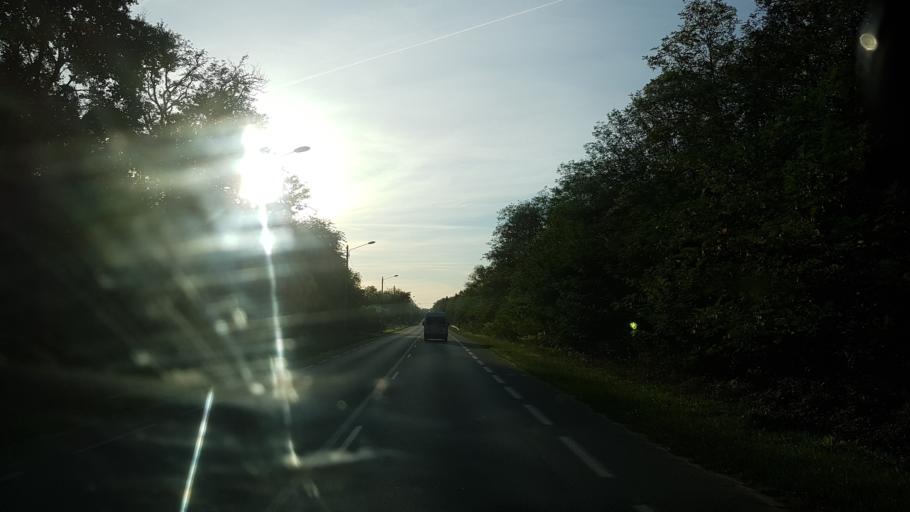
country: FR
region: Aquitaine
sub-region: Departement de la Gironde
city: Saint-Medard-en-Jalles
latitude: 44.8455
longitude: -0.7271
